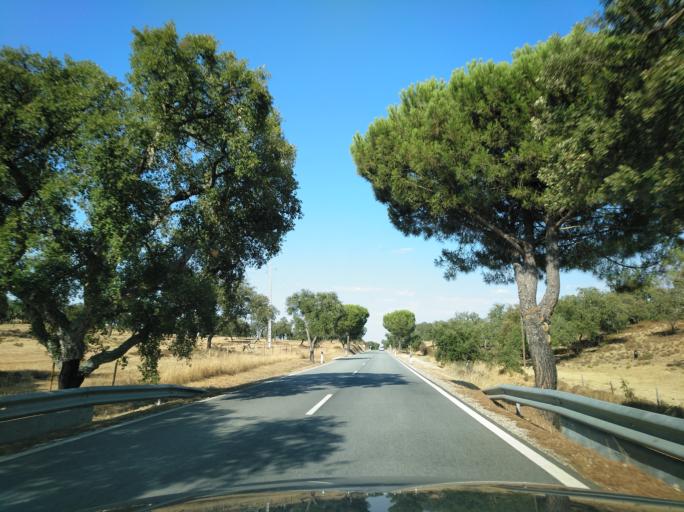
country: ES
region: Andalusia
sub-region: Provincia de Huelva
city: Rosal de la Frontera
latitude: 38.0093
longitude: -7.2767
